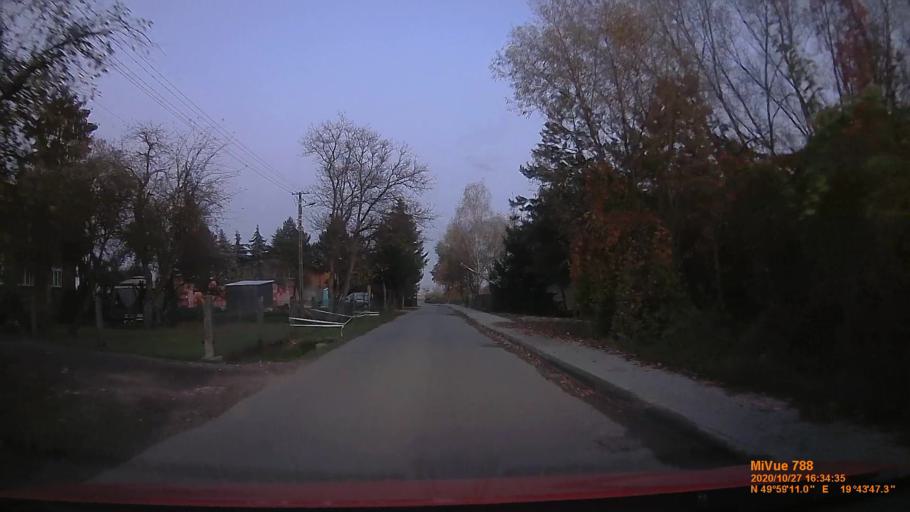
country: PL
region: Lesser Poland Voivodeship
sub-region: Powiat krakowski
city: Wolowice
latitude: 49.9864
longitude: 19.7298
